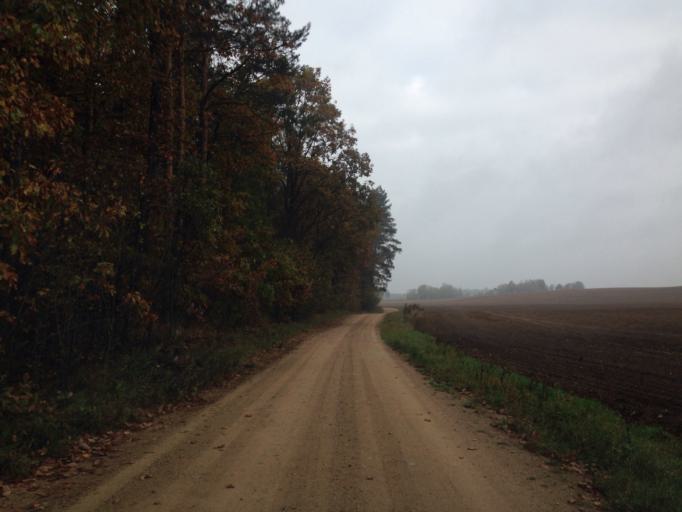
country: PL
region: Warmian-Masurian Voivodeship
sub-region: Powiat dzialdowski
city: Lidzbark
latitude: 53.2598
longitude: 19.7519
